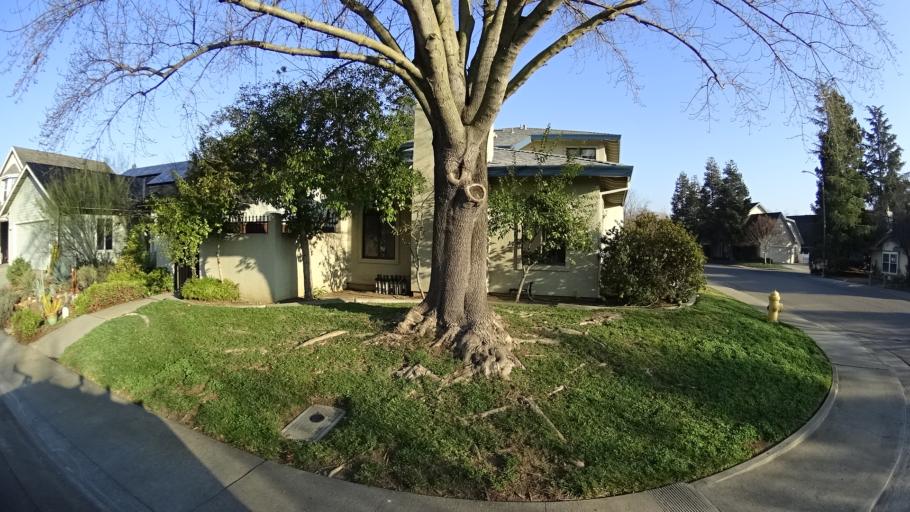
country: US
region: California
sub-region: Yolo County
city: Davis
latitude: 38.5579
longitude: -121.7850
